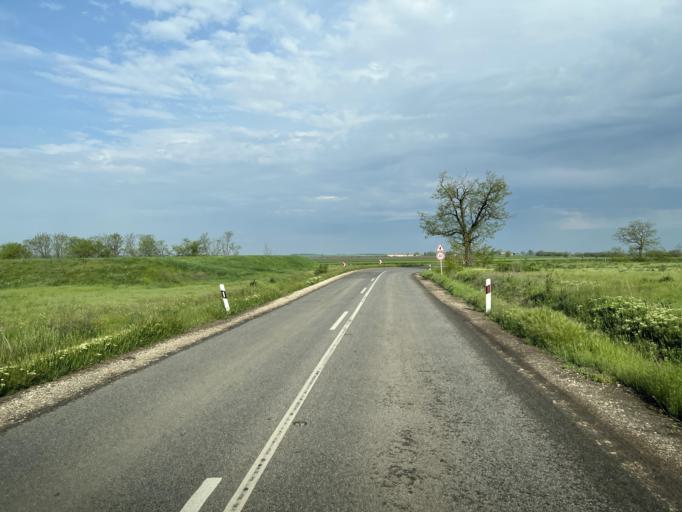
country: HU
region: Pest
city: Tapioszentmarton
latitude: 47.3191
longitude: 19.7481
